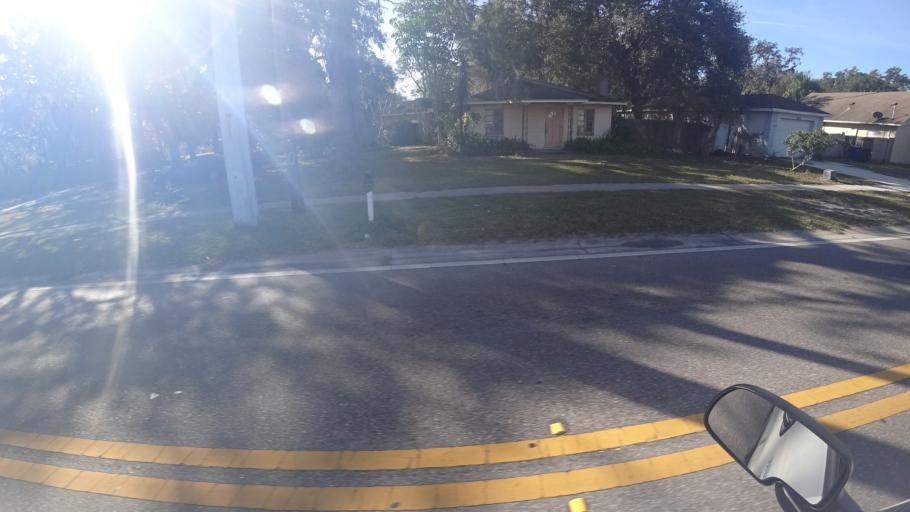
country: US
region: Florida
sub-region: Manatee County
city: West Samoset
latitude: 27.4770
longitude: -82.5601
